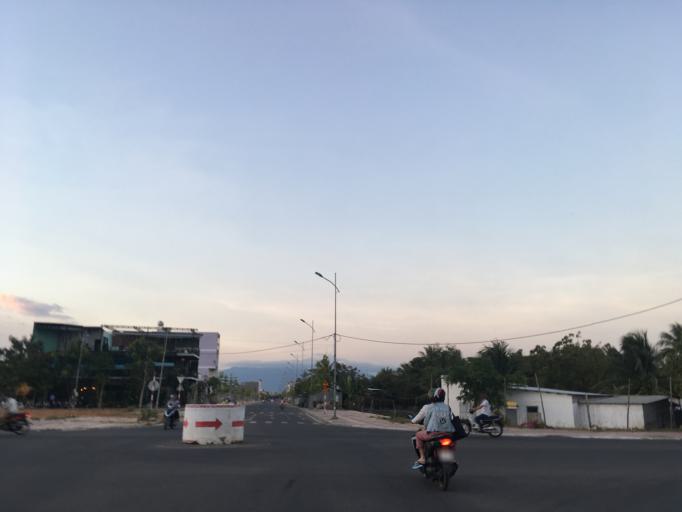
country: VN
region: Ninh Thuan
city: Phan Rang-Thap Cham
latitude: 11.5707
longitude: 108.9985
